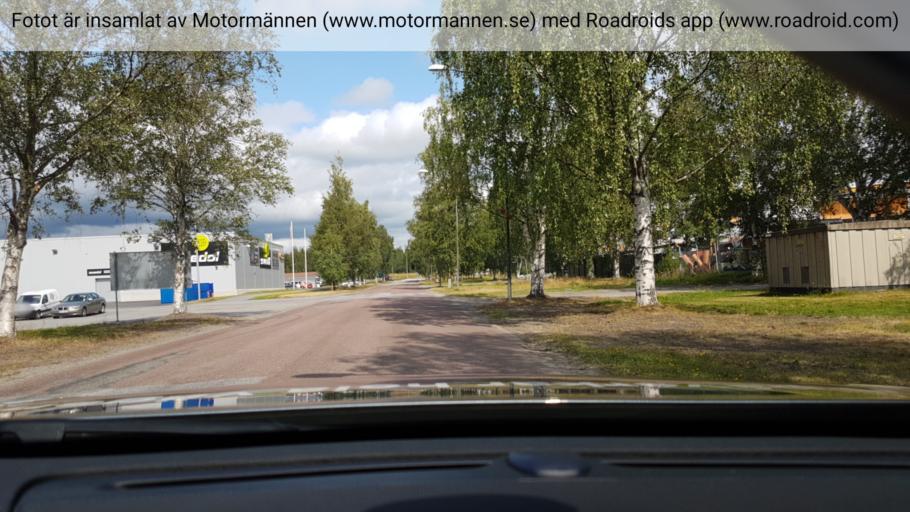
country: SE
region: Vaesterbotten
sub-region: Umea Kommun
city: Umea
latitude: 63.8393
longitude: 20.2381
